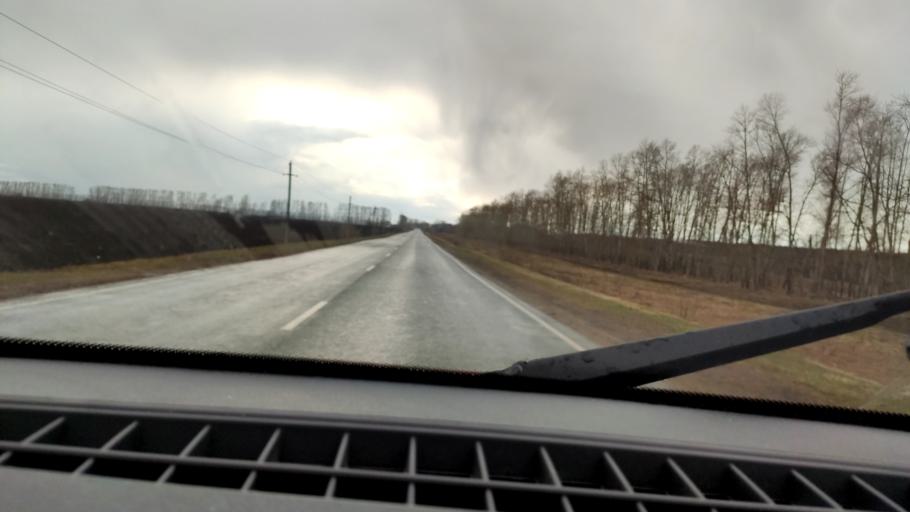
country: RU
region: Bashkortostan
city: Kushnarenkovo
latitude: 55.0613
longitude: 55.2102
